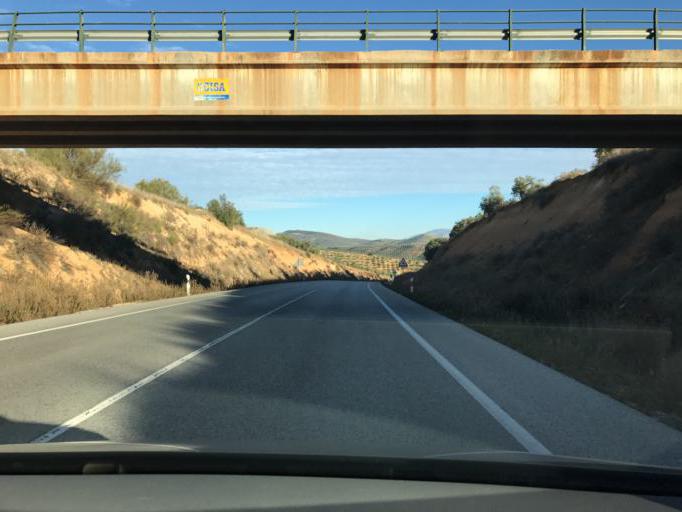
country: ES
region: Andalusia
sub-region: Provincia de Granada
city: Iznalloz
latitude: 37.4025
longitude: -3.5354
